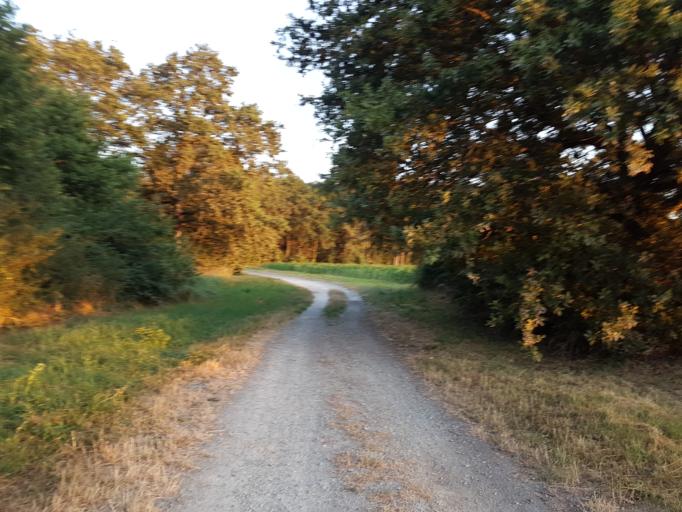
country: FR
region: Centre
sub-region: Departement d'Indre-et-Loire
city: Saint-Avertin
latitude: 47.3519
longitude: 0.7602
